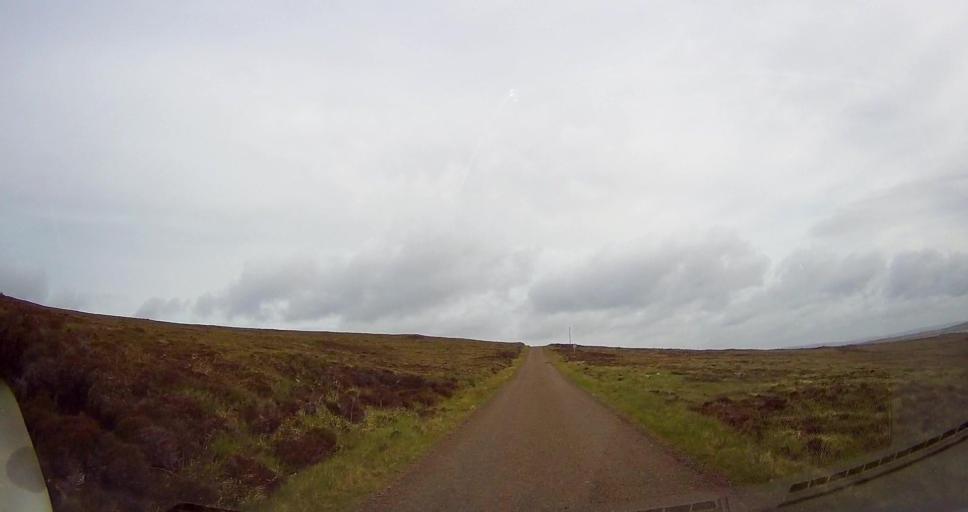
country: GB
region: Scotland
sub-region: Orkney Islands
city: Stromness
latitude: 58.8629
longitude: -3.2220
